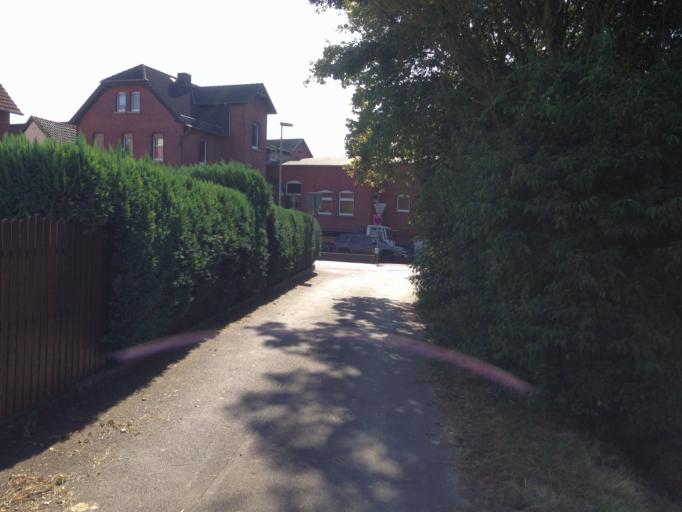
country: DE
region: Hesse
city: Staufenberg
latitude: 50.6524
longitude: 8.7382
